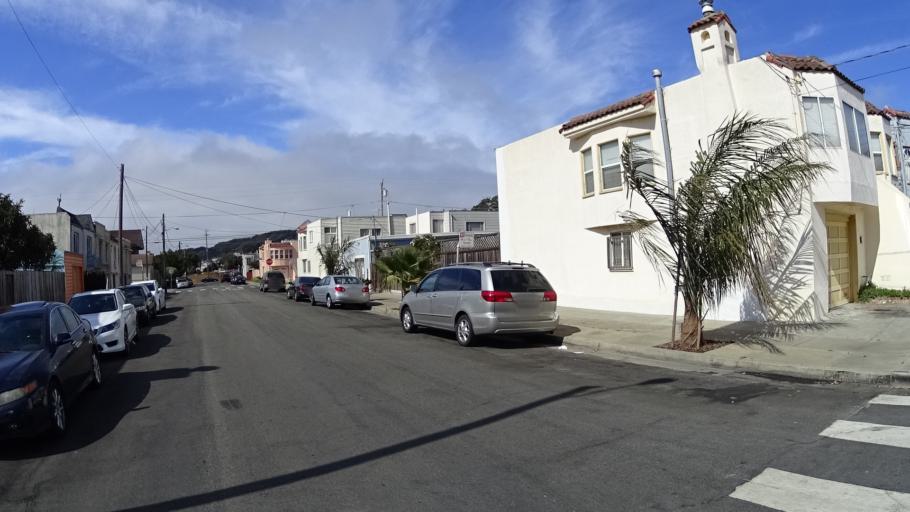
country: US
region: California
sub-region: San Mateo County
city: Brisbane
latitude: 37.7107
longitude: -122.3995
